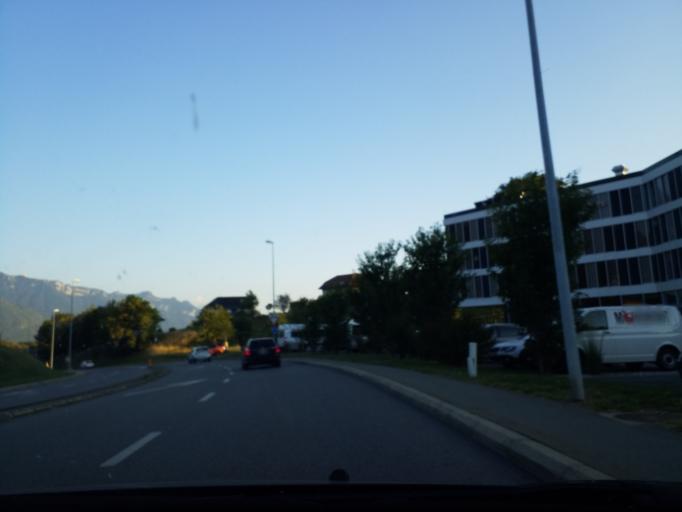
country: CH
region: Vaud
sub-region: Riviera-Pays-d'Enhaut District
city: La Tour-de-Peilz
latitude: 46.4693
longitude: 6.8632
